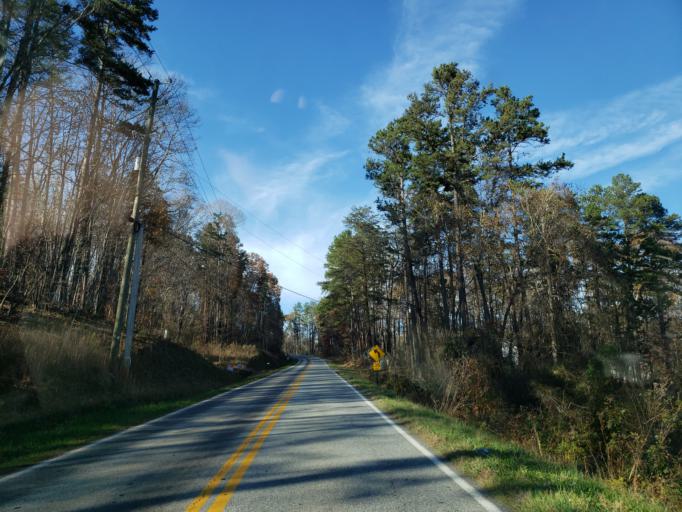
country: US
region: Georgia
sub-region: Lumpkin County
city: Dahlonega
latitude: 34.4590
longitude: -84.0025
